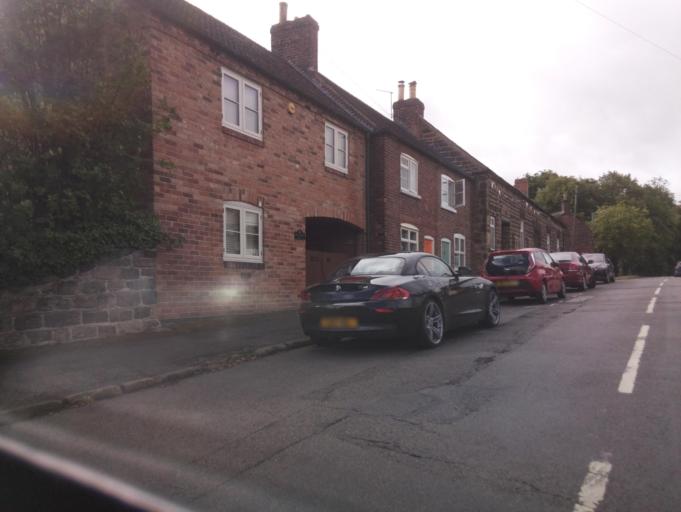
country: GB
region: England
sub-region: Derbyshire
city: Ilkeston
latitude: 52.9376
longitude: -1.3091
